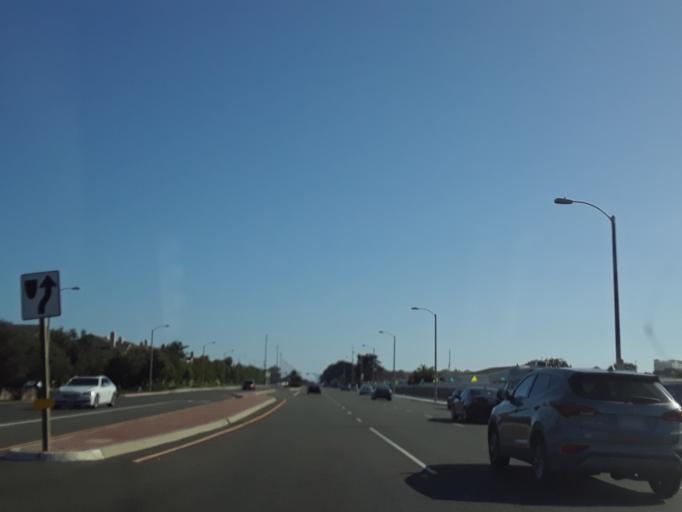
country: US
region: California
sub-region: Orange County
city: Huntington Beach
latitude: 33.6620
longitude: -117.9885
